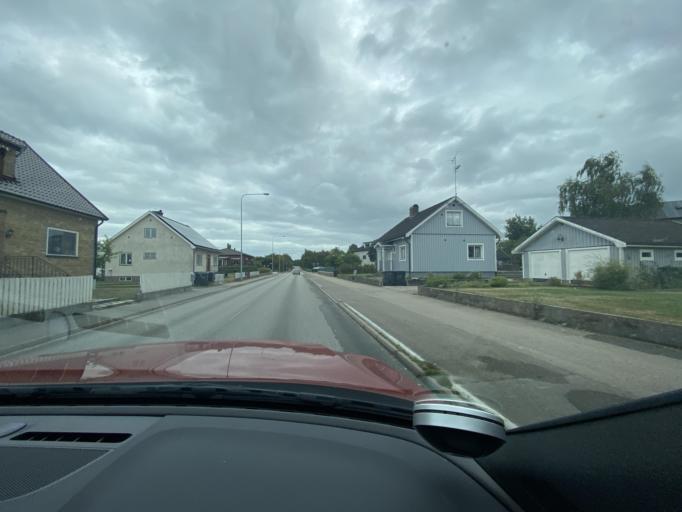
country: SE
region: Kronoberg
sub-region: Markaryds Kommun
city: Markaryd
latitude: 56.4613
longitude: 13.6010
